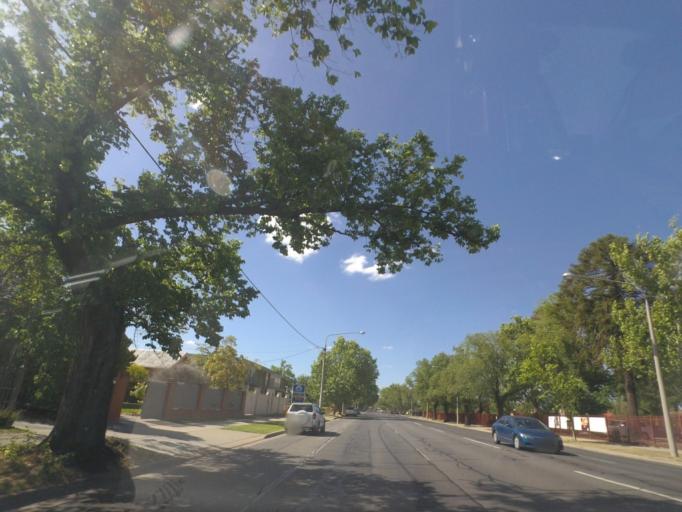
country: AU
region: New South Wales
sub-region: Albury Municipality
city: Albury
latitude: -36.0732
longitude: 146.9256
